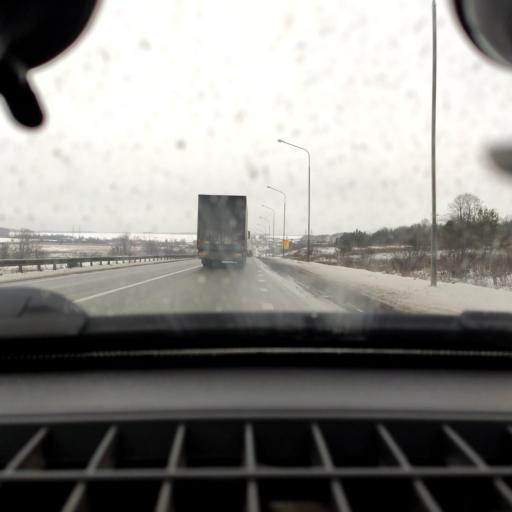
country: RU
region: Bashkortostan
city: Iglino
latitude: 54.7638
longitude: 56.4108
